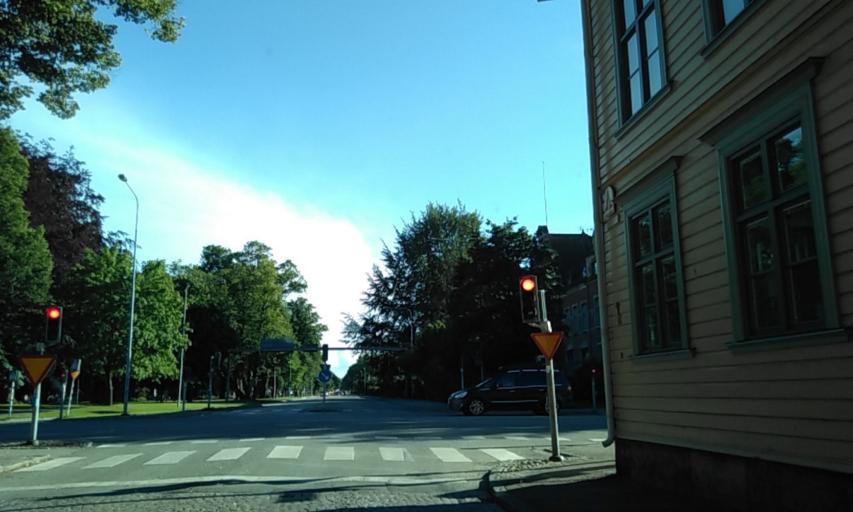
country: SE
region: Vaestra Goetaland
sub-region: Lidkopings Kommun
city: Lidkoping
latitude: 58.5017
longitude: 13.1544
